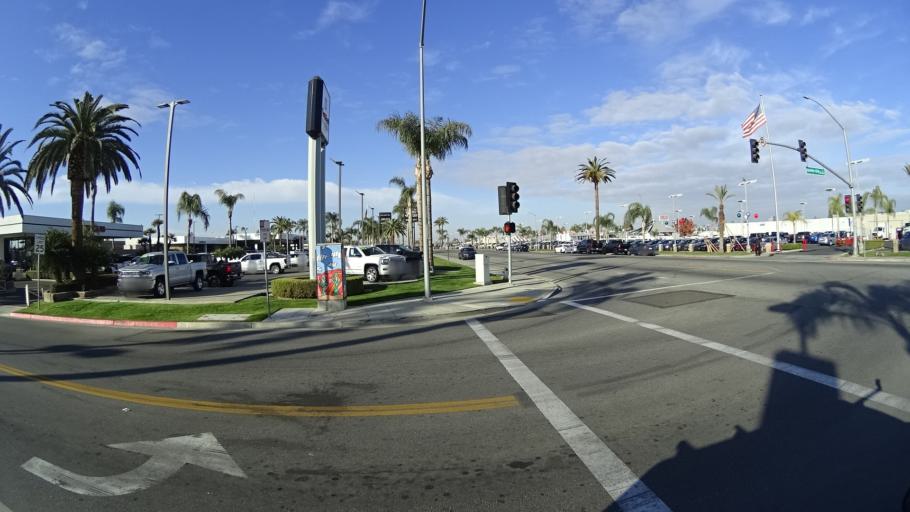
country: US
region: California
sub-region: Kern County
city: Greenfield
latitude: 35.3102
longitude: -119.0354
